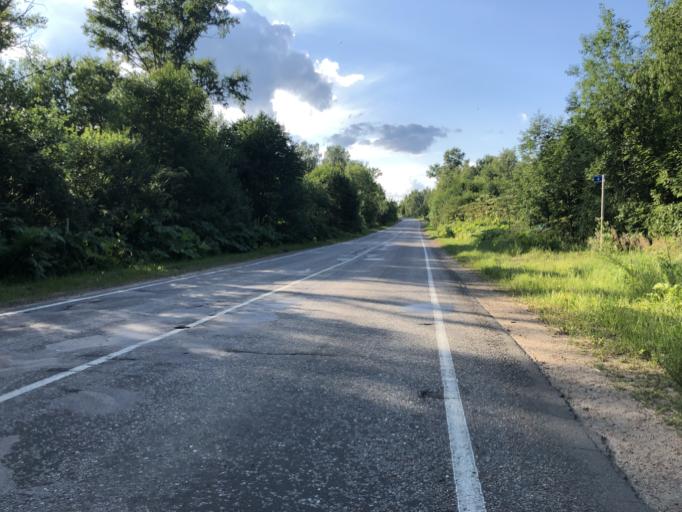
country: RU
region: Tverskaya
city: Rzhev
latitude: 56.2704
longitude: 34.2474
